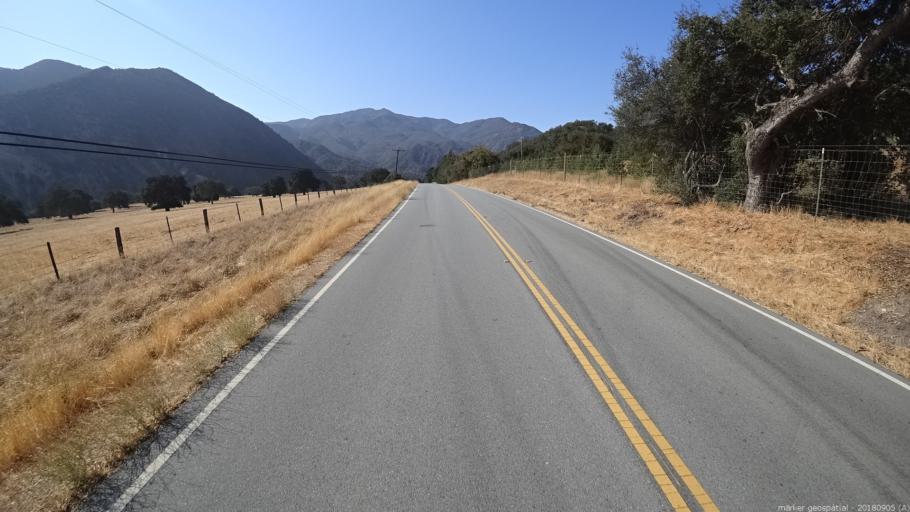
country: US
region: California
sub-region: Monterey County
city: Greenfield
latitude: 36.2487
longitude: -121.4323
